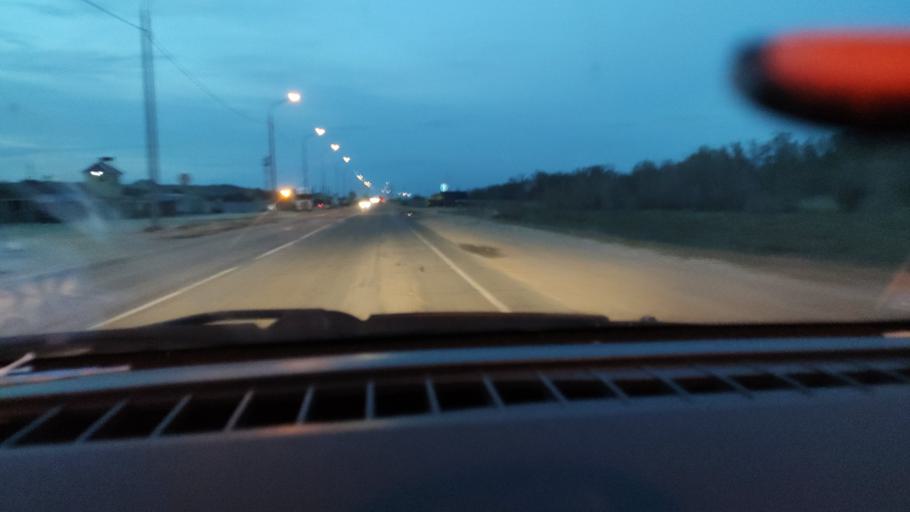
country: RU
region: Saratov
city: Sinodskoye
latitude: 52.0857
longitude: 46.8019
